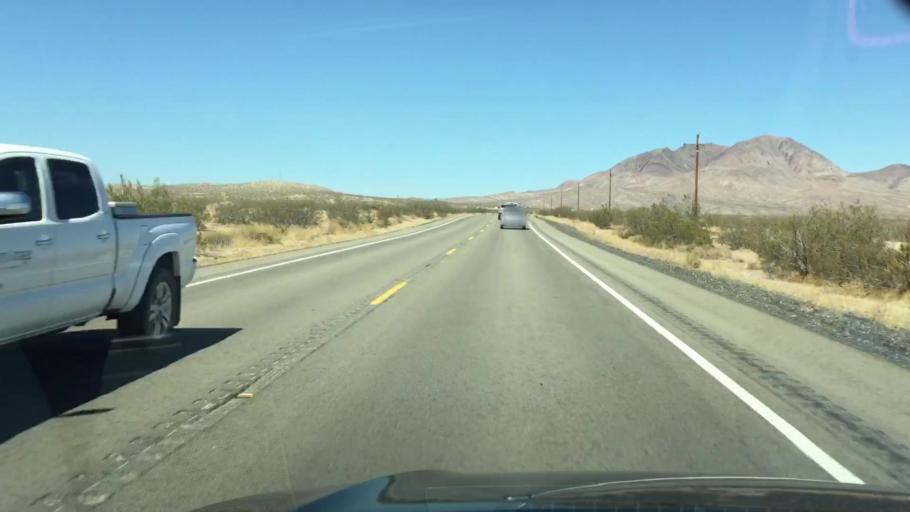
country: US
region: California
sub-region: Kern County
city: Boron
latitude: 35.2926
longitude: -117.6151
